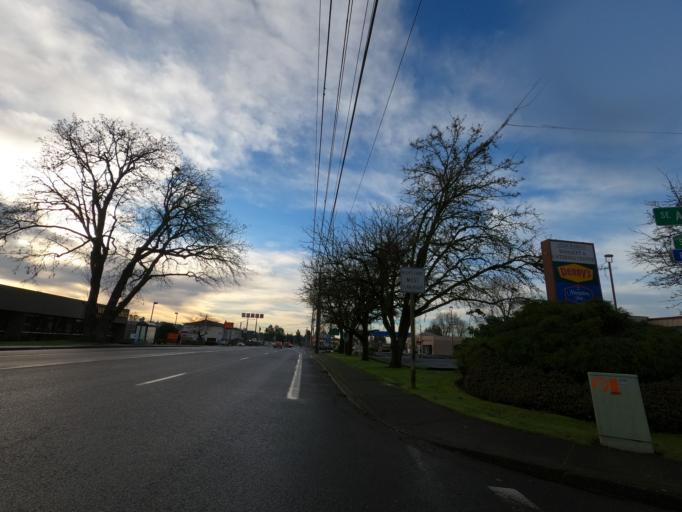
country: US
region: Oregon
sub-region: Clackamas County
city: Clackamas
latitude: 45.4088
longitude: -122.5690
